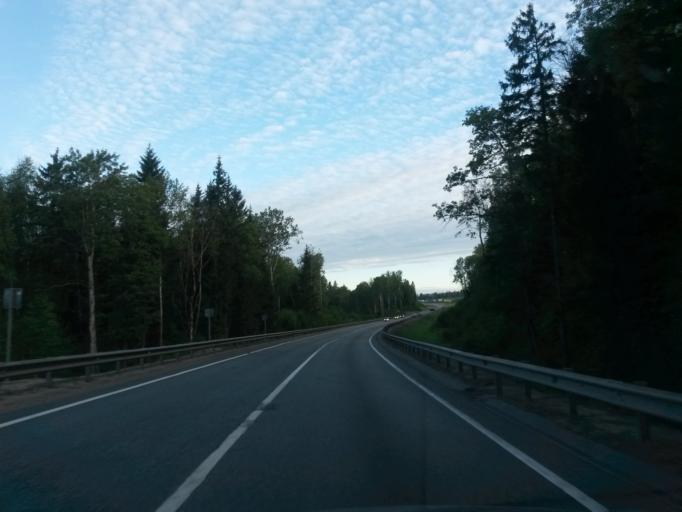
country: RU
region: Vladimir
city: Strunino
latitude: 56.5515
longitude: 38.5896
